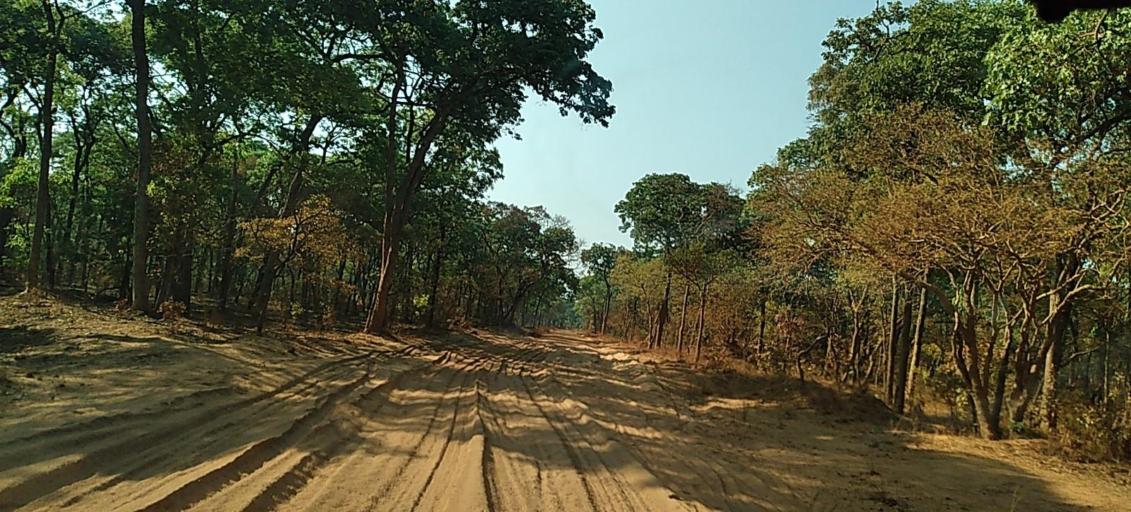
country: ZM
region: North-Western
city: Kasempa
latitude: -13.6536
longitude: 26.0064
